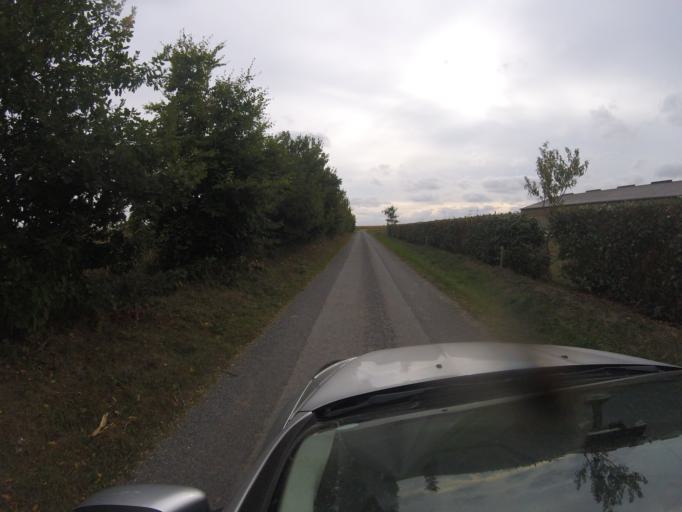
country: FR
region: Lower Normandy
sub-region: Departement de la Manche
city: Le Val-Saint-Pere
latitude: 48.6335
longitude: -1.3982
